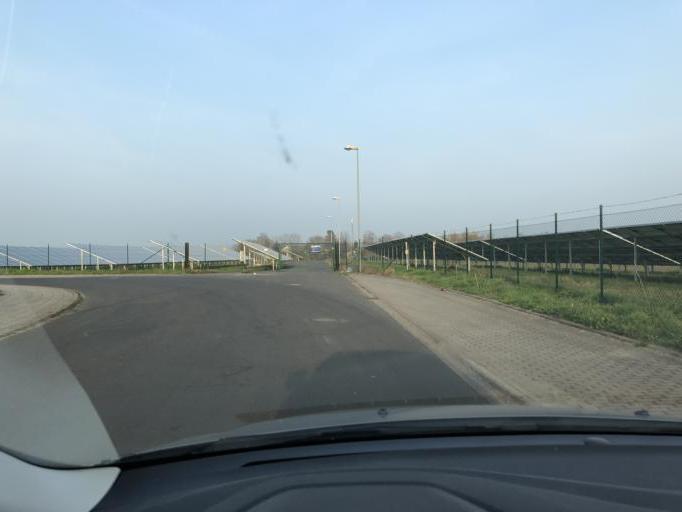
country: DE
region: Saxony
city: Rackwitz
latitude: 51.4033
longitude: 12.3612
